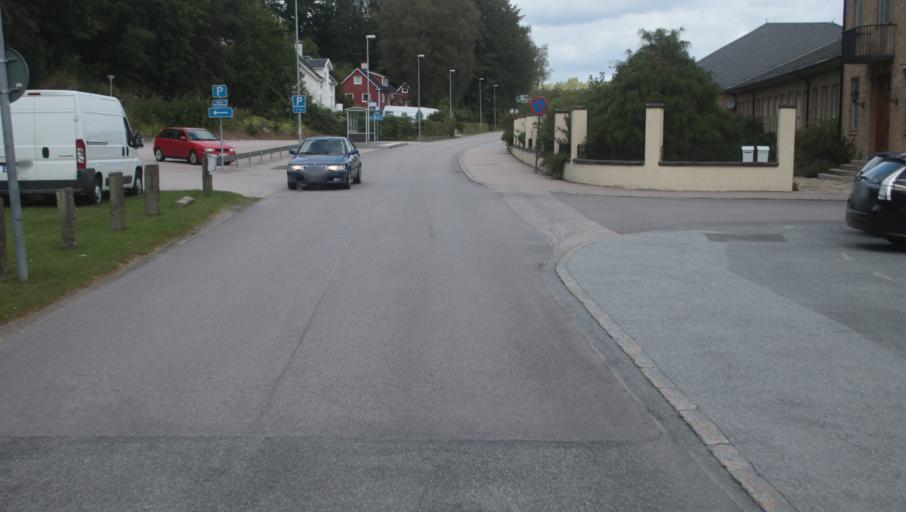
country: SE
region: Blekinge
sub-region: Karlshamns Kommun
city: Svangsta
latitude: 56.2608
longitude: 14.7687
